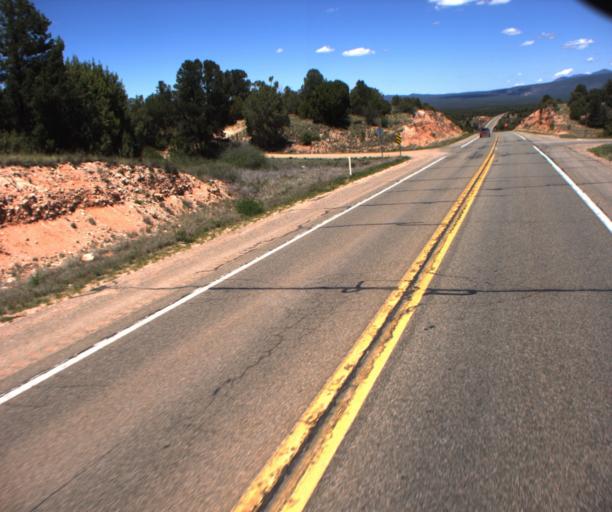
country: US
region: Arizona
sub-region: Yavapai County
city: Paulden
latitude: 34.9734
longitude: -112.4056
